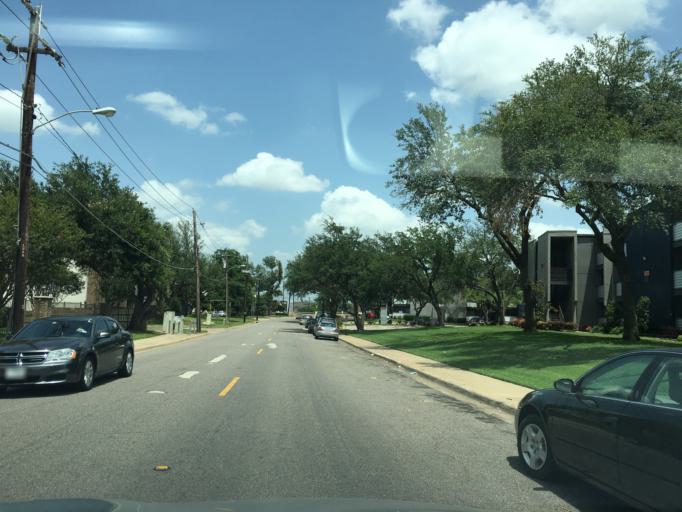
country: US
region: Texas
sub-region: Dallas County
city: University Park
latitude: 32.8959
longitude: -96.7720
